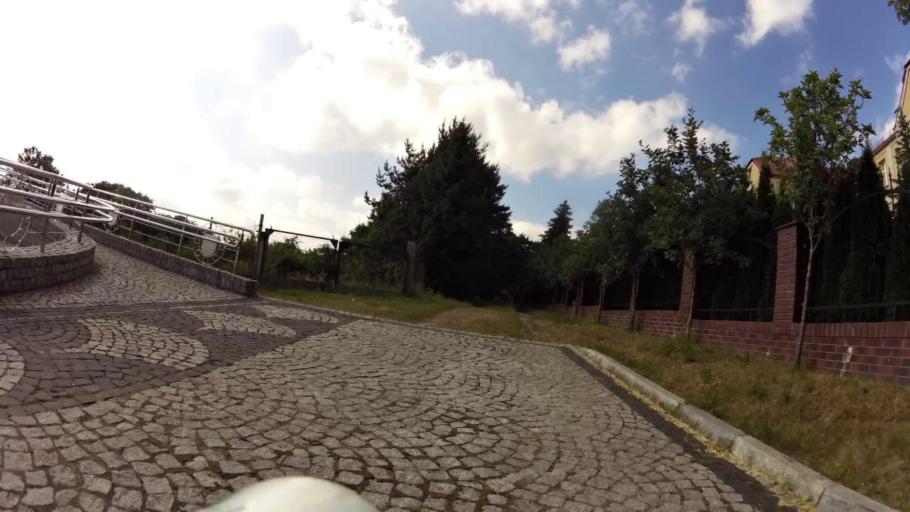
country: PL
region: West Pomeranian Voivodeship
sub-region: Powiat koszalinski
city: Bobolice
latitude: 53.9560
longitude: 16.5885
